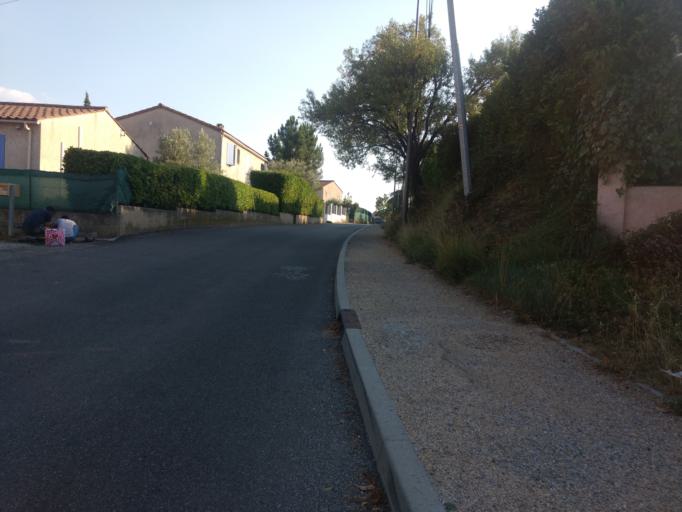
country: FR
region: Provence-Alpes-Cote d'Azur
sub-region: Departement des Alpes-de-Haute-Provence
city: Manosque
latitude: 43.8229
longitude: 5.7749
